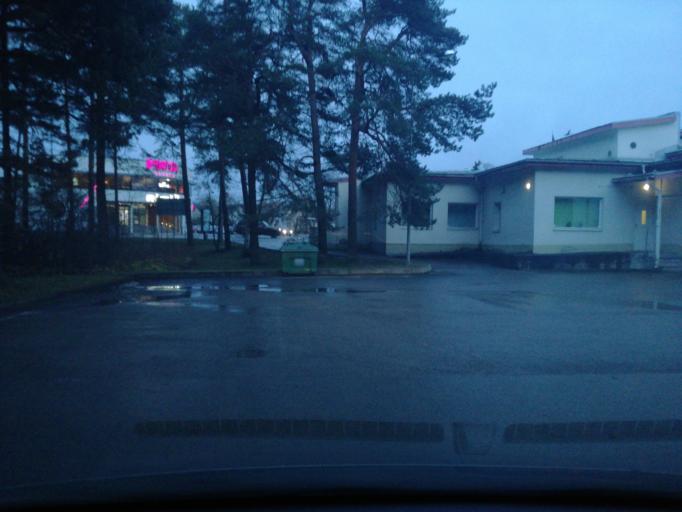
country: EE
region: Harju
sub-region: Viimsi vald
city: Viimsi
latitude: 59.4683
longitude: 24.8333
